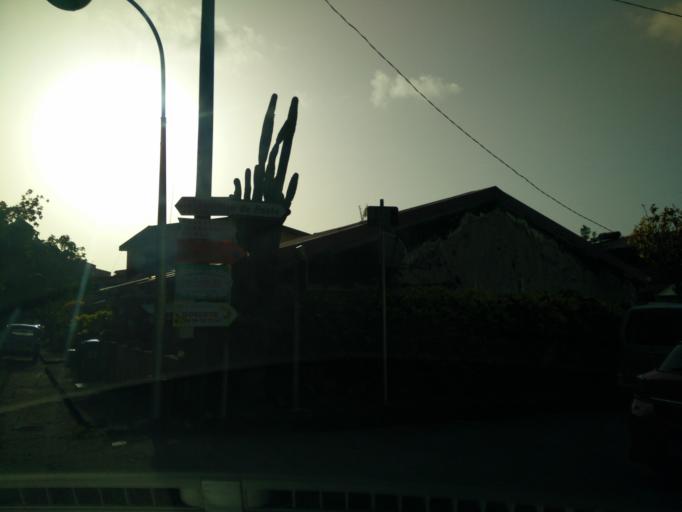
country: MQ
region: Martinique
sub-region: Martinique
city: Basse-Pointe
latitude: 14.8726
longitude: -61.1783
